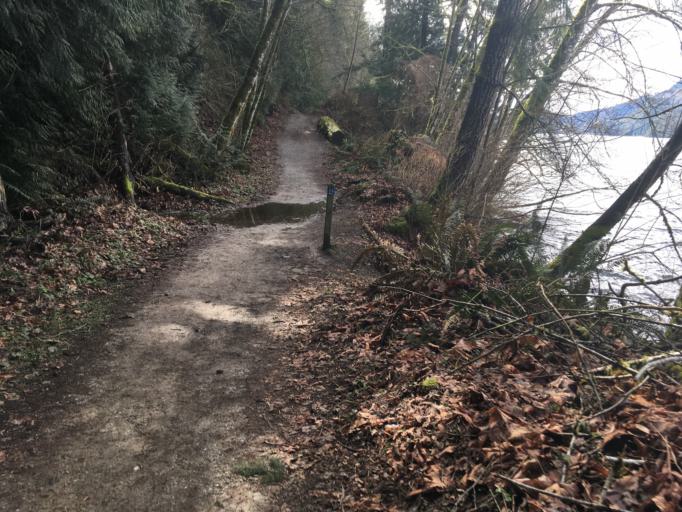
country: US
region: Washington
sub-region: Whatcom County
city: Sudden Valley
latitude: 48.7038
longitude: -122.2977
